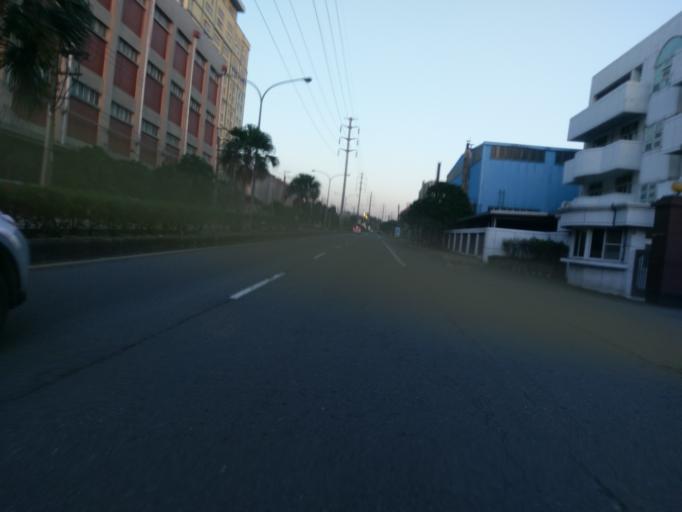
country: TW
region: Taiwan
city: Taoyuan City
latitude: 25.0551
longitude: 121.1285
